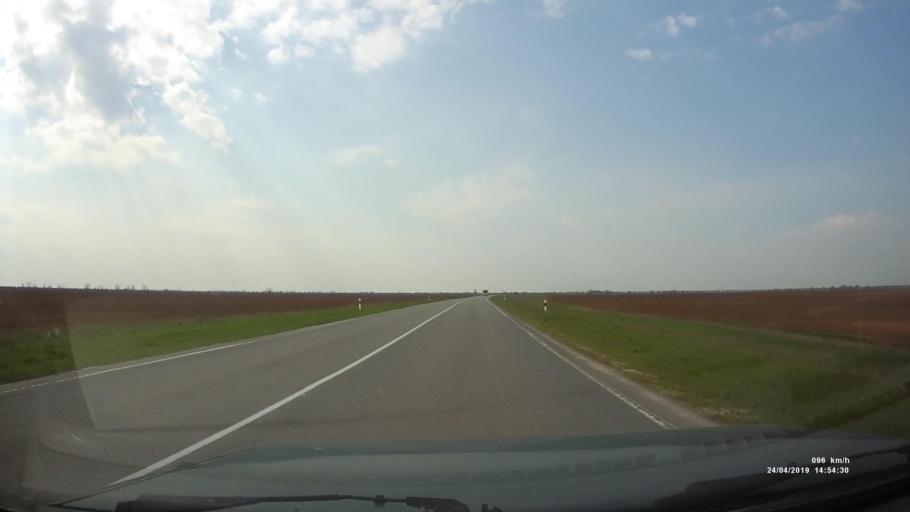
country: RU
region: Rostov
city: Remontnoye
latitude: 46.5348
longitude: 43.6376
